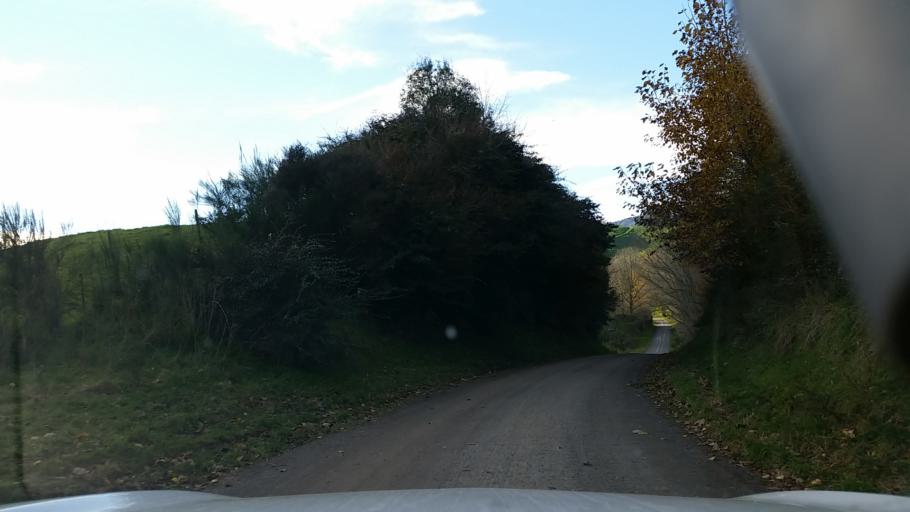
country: NZ
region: Bay of Plenty
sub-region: Rotorua District
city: Rotorua
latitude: -38.3879
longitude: 176.1914
